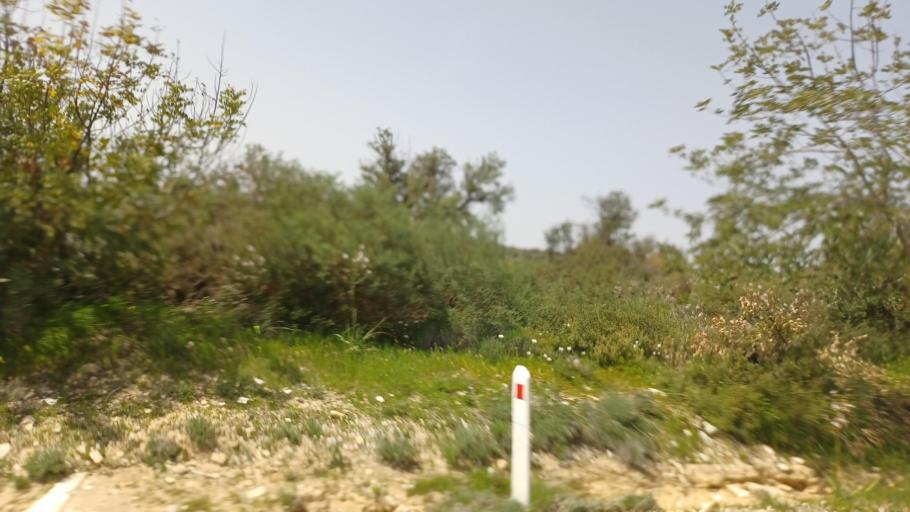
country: CY
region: Limassol
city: Pissouri
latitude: 34.7245
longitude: 32.7375
